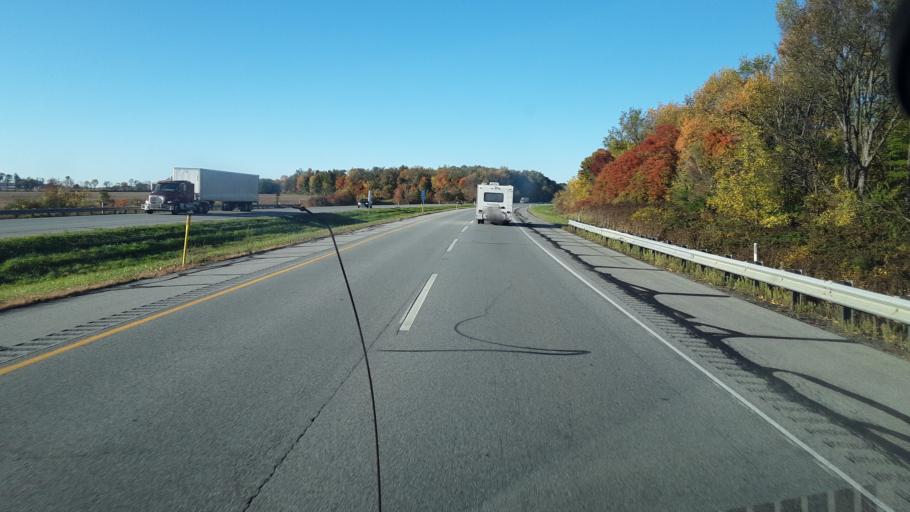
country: US
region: Indiana
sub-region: LaPorte County
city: LaPorte
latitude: 41.6276
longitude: -86.7984
